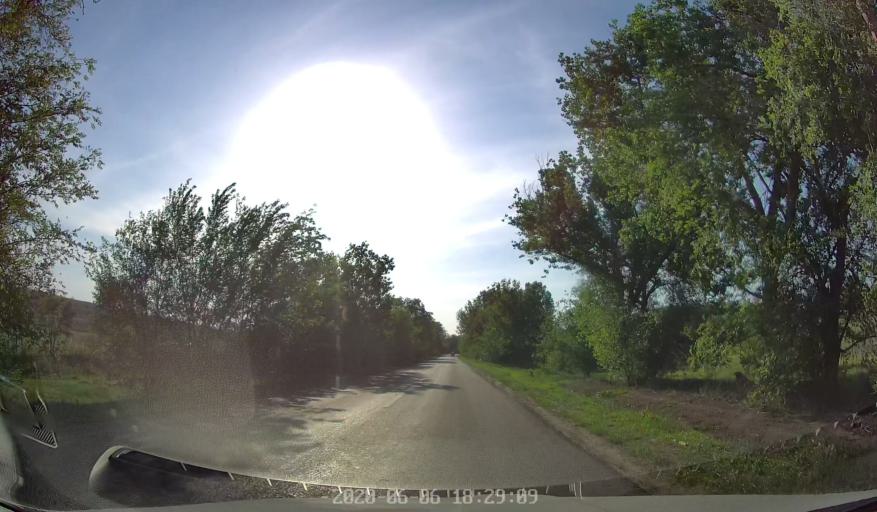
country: MD
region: Chisinau
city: Ciorescu
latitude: 47.1312
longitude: 28.9742
